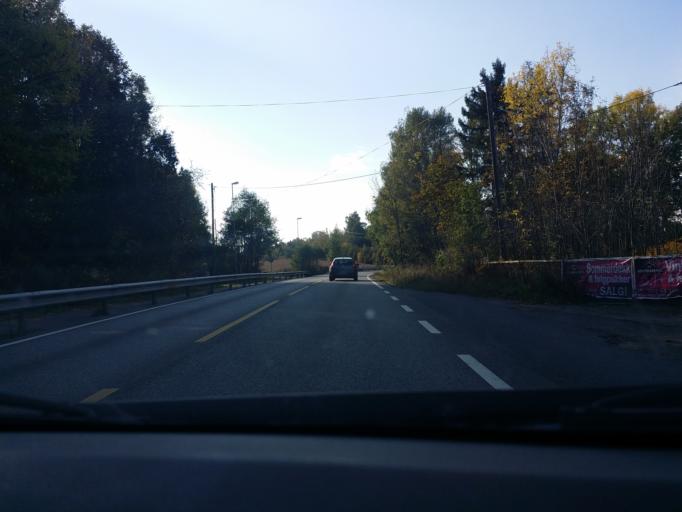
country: NO
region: Buskerud
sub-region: Hole
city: Vik
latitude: 60.0577
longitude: 10.3032
